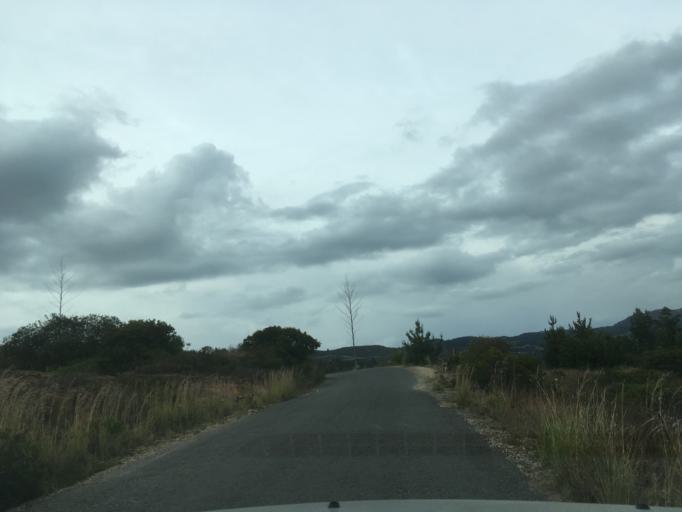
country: CO
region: Boyaca
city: Firavitoba
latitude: 5.6760
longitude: -73.0181
